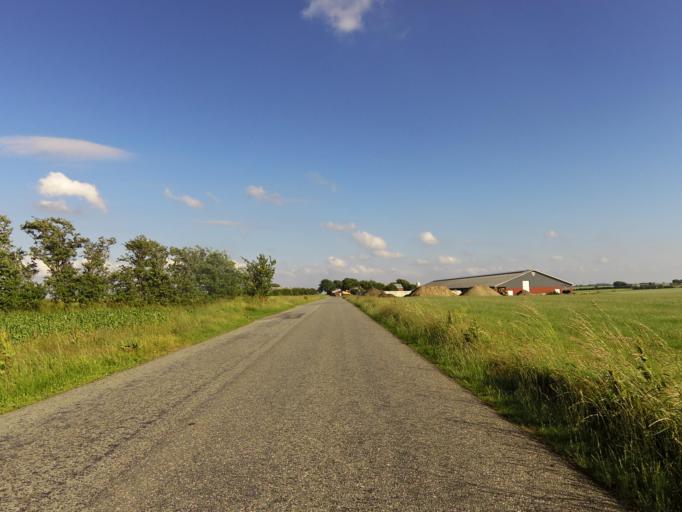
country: DK
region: South Denmark
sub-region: Vejen Kommune
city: Rodding
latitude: 55.3405
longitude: 9.1507
